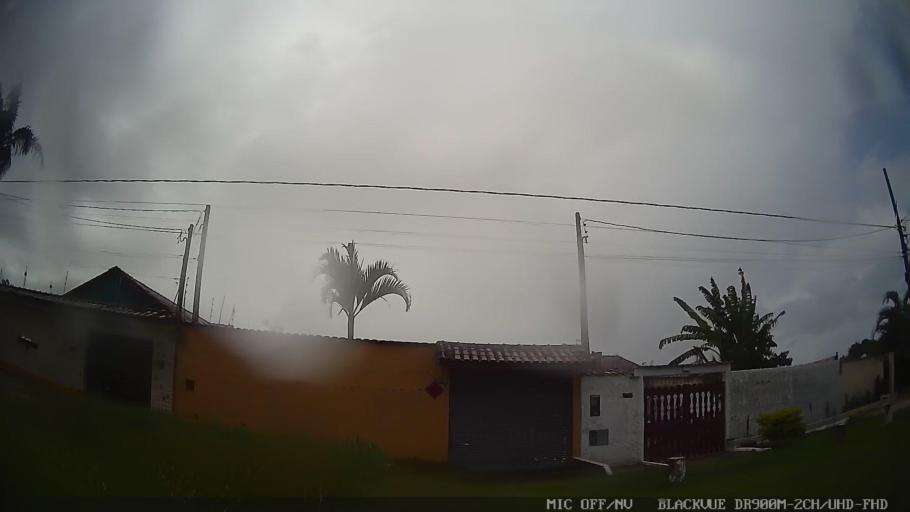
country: BR
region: Sao Paulo
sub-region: Itanhaem
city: Itanhaem
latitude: -24.2142
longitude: -46.8666
